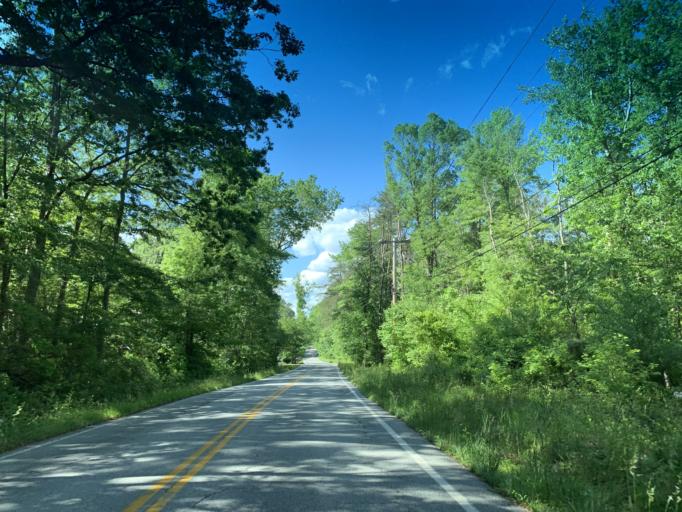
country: US
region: Maryland
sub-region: Cecil County
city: North East
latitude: 39.5685
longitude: -75.9392
